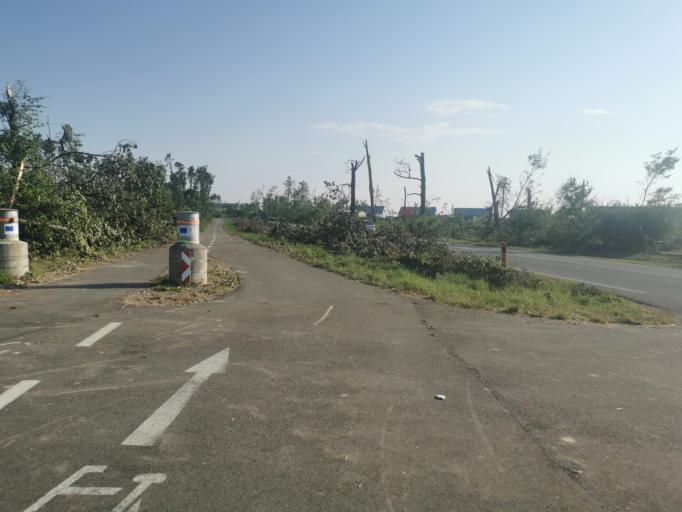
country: CZ
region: South Moravian
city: Rohatec
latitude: 48.8867
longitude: 17.1486
